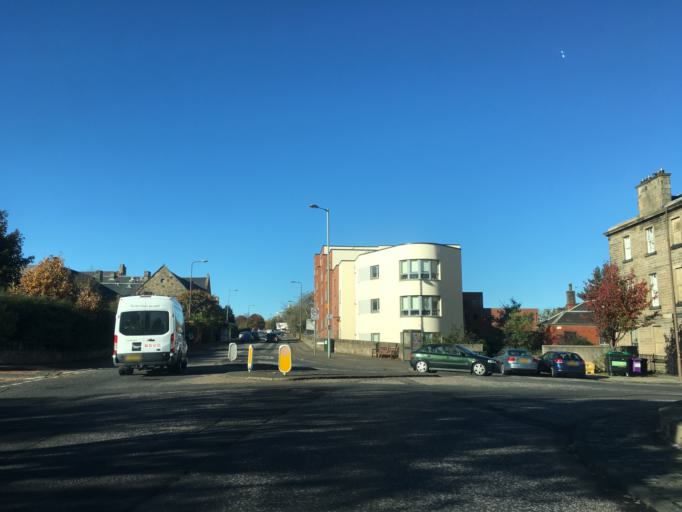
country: GB
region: Scotland
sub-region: Edinburgh
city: Edinburgh
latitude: 55.9806
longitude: -3.2245
